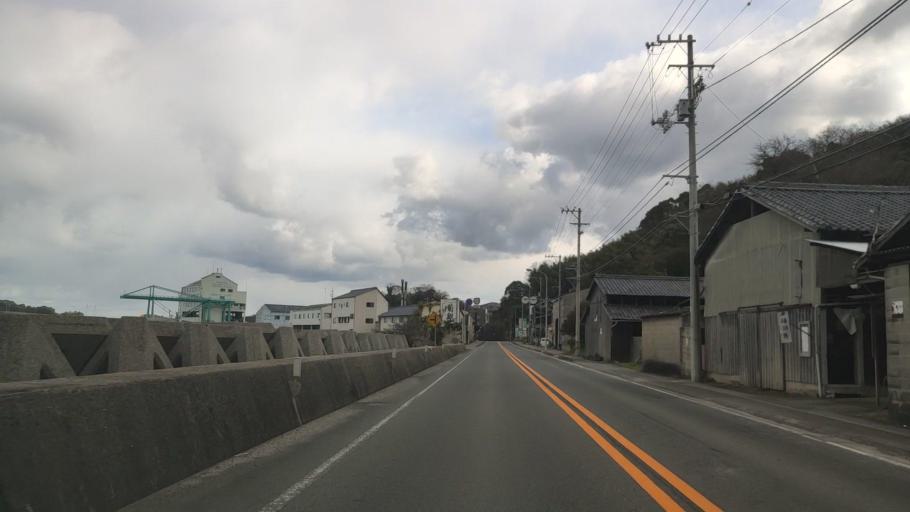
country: JP
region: Ehime
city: Hojo
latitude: 34.0326
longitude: 132.8336
